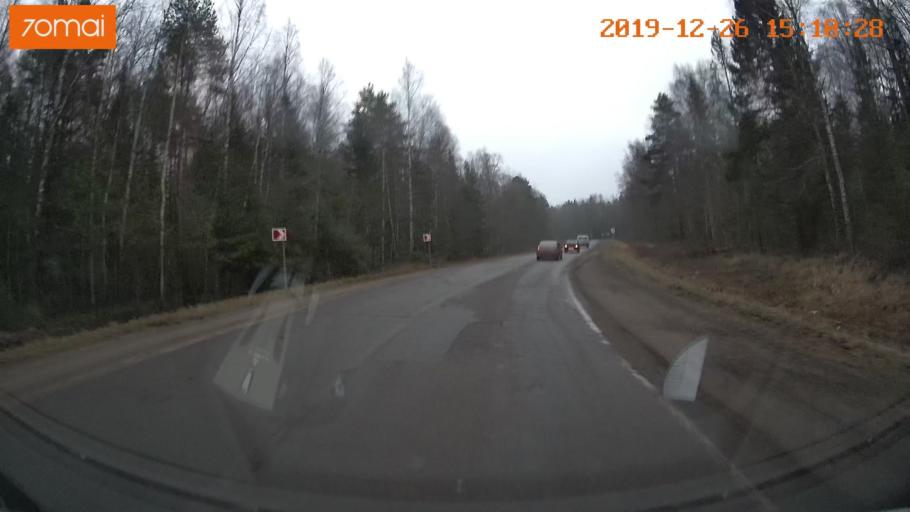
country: RU
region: Jaroslavl
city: Rybinsk
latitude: 58.1401
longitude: 38.8521
